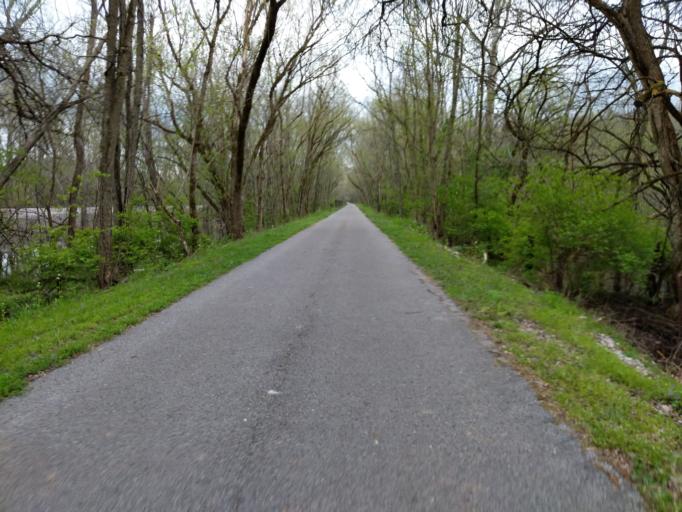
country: US
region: Ohio
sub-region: Athens County
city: The Plains
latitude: 39.3772
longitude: -82.1150
